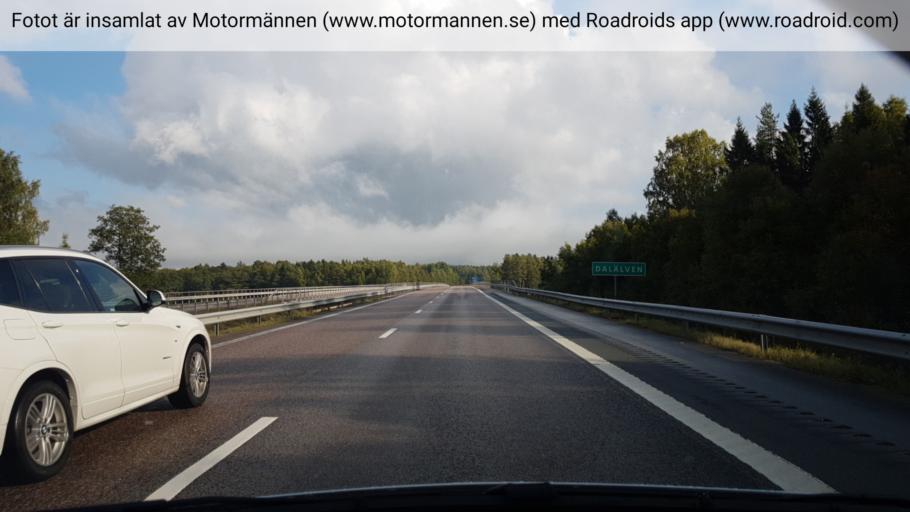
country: SE
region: Uppsala
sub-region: Alvkarleby Kommun
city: AElvkarleby
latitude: 60.4718
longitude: 17.3911
